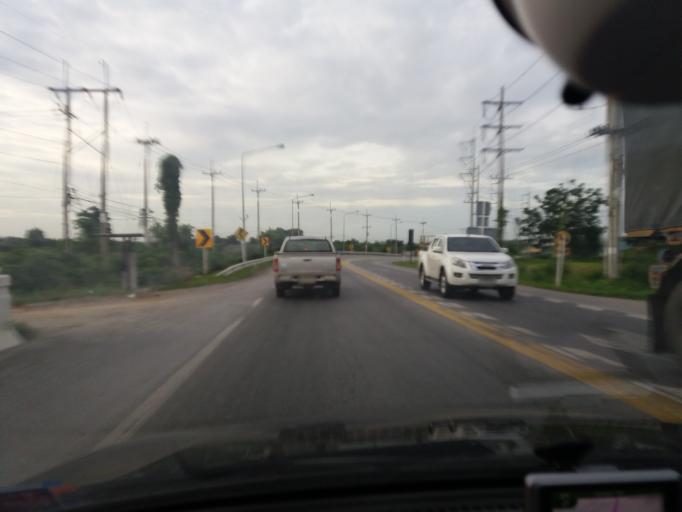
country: TH
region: Suphan Buri
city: U Thong
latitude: 14.5120
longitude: 99.9157
